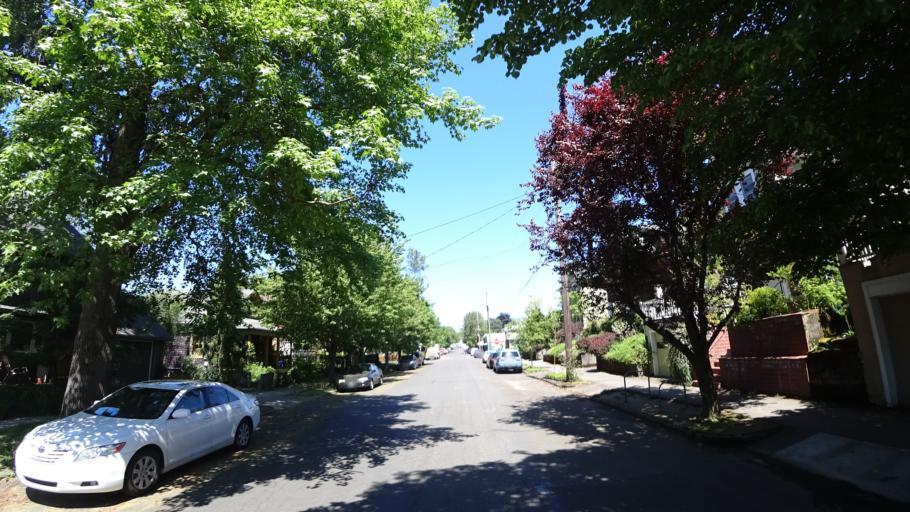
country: US
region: Oregon
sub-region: Multnomah County
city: Portland
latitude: 45.5022
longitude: -122.6404
